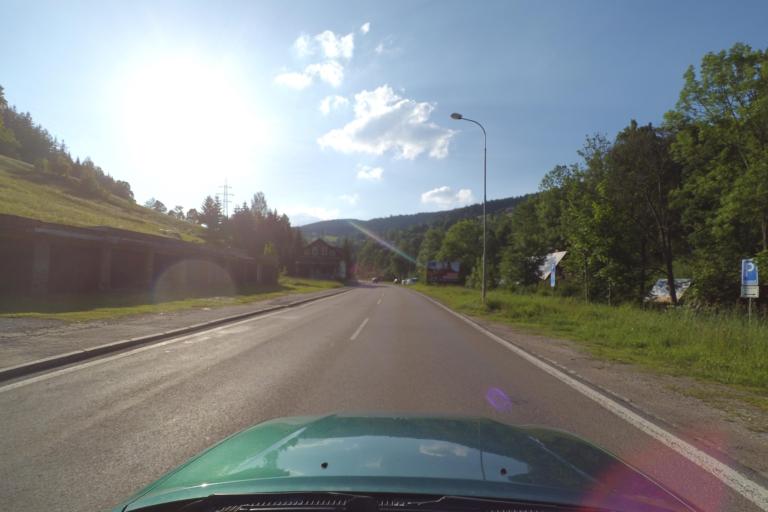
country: CZ
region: Kralovehradecky
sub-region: Okres Trutnov
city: Svoboda nad Upou
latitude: 50.6891
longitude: 15.7781
